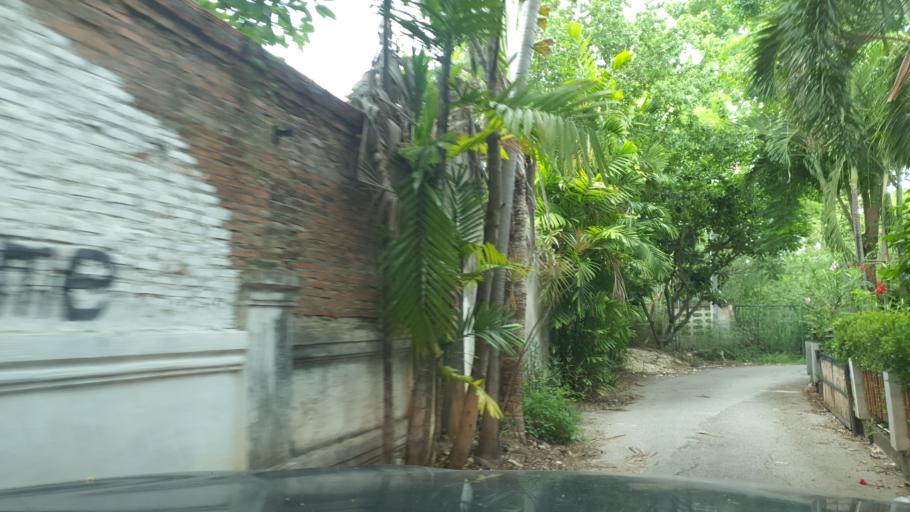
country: TH
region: Lampang
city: Lampang
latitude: 18.2831
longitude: 99.5045
